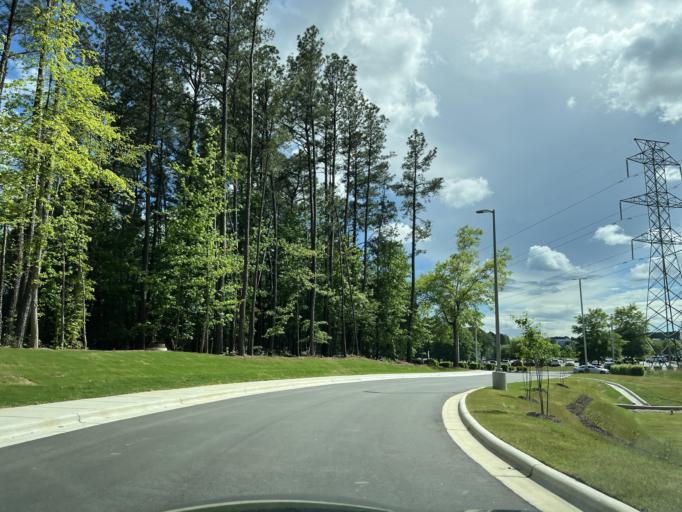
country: US
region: North Carolina
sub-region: Wake County
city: Wake Forest
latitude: 35.8912
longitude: -78.5623
